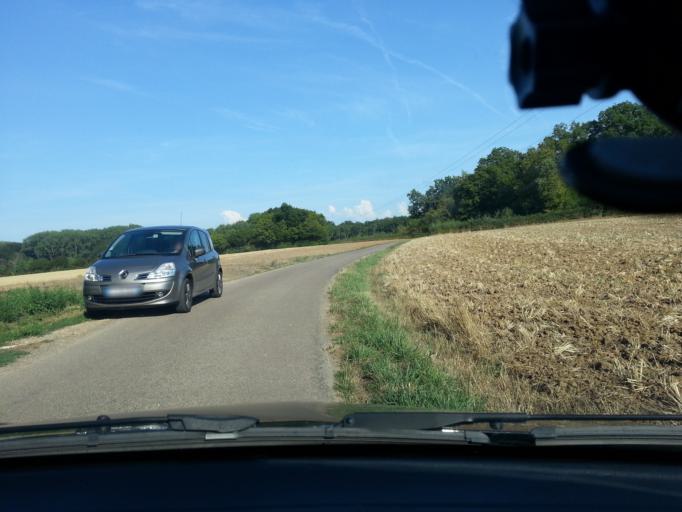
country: FR
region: Bourgogne
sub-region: Departement de Saone-et-Loire
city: Dracy-le-Fort
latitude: 46.7771
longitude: 4.7779
